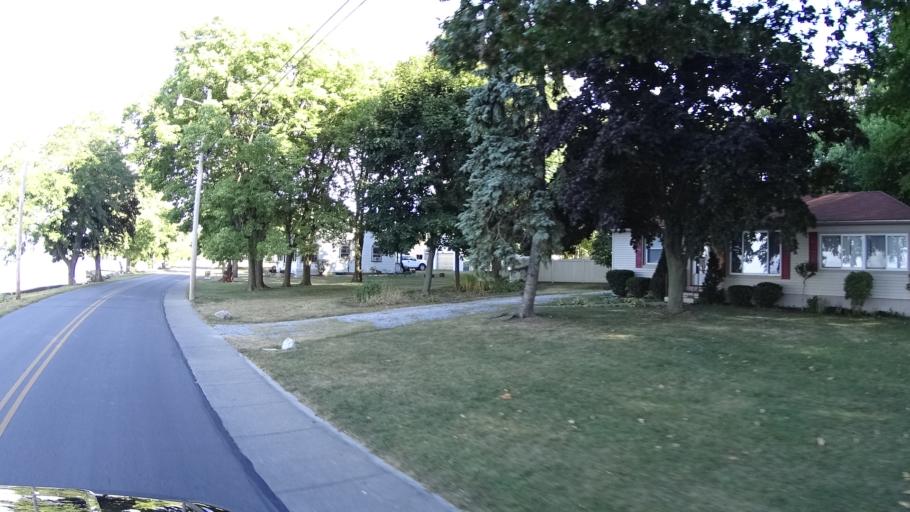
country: US
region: Ohio
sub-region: Erie County
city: Sandusky
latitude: 41.5965
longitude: -82.7265
